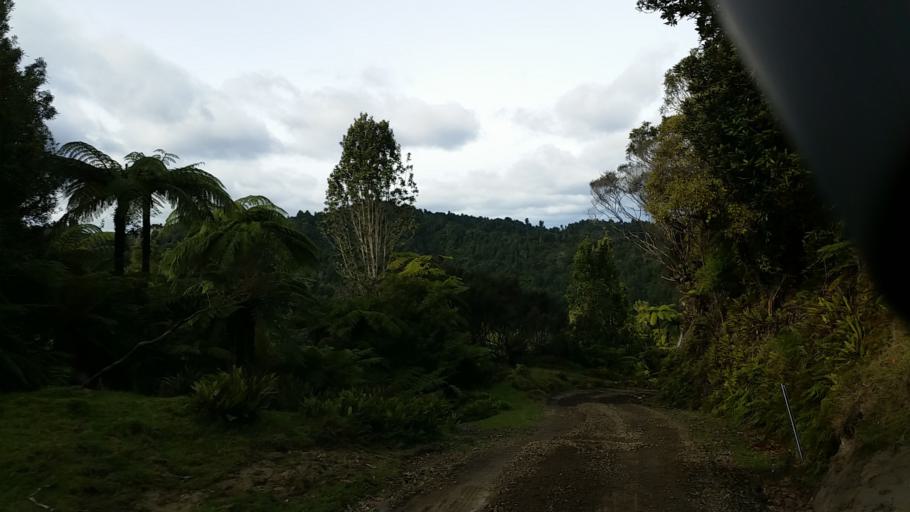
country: NZ
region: Taranaki
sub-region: New Plymouth District
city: Waitara
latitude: -39.0515
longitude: 174.6113
